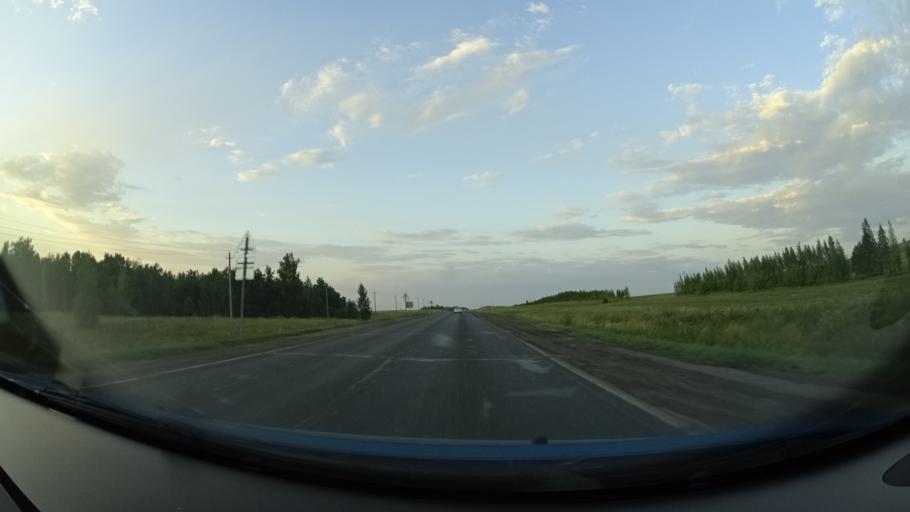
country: RU
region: Orenburg
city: Severnoye
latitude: 54.2000
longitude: 52.6881
